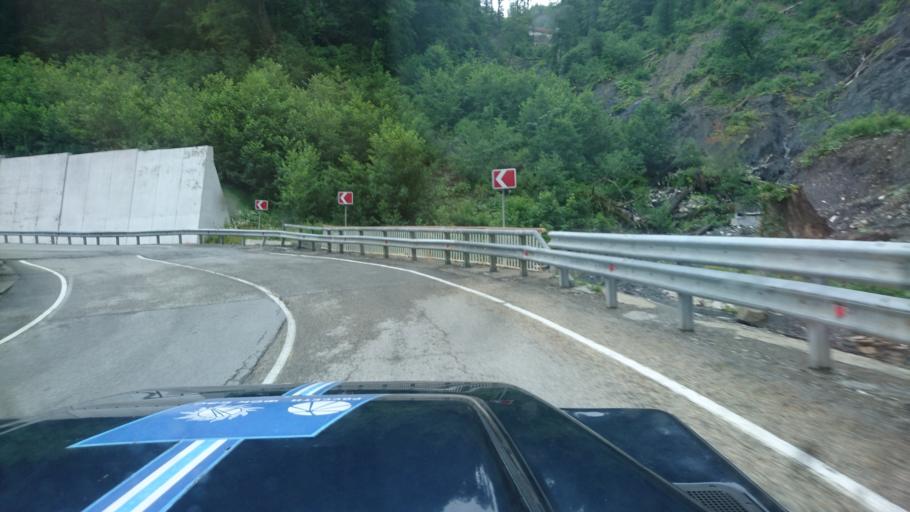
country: RU
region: Krasnodarskiy
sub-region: Sochi City
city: Krasnaya Polyana
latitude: 43.6604
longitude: 40.3109
